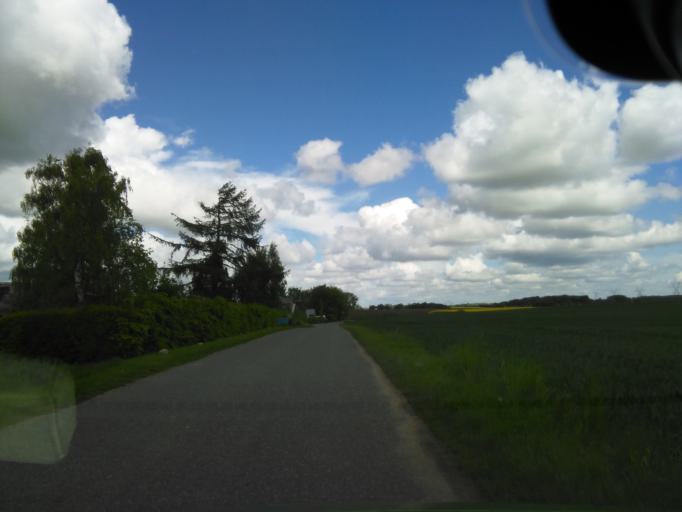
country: DK
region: Central Jutland
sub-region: Arhus Kommune
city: Solbjerg
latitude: 56.0184
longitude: 10.1195
